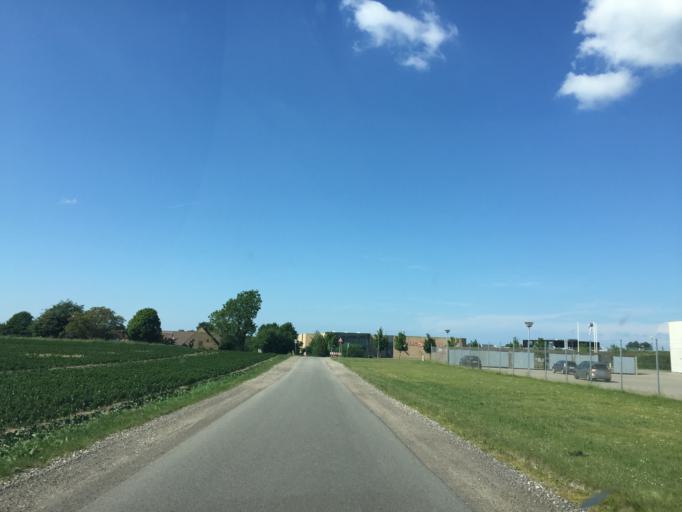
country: DK
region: South Denmark
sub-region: Odense Kommune
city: Hojby
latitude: 55.3436
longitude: 10.3971
